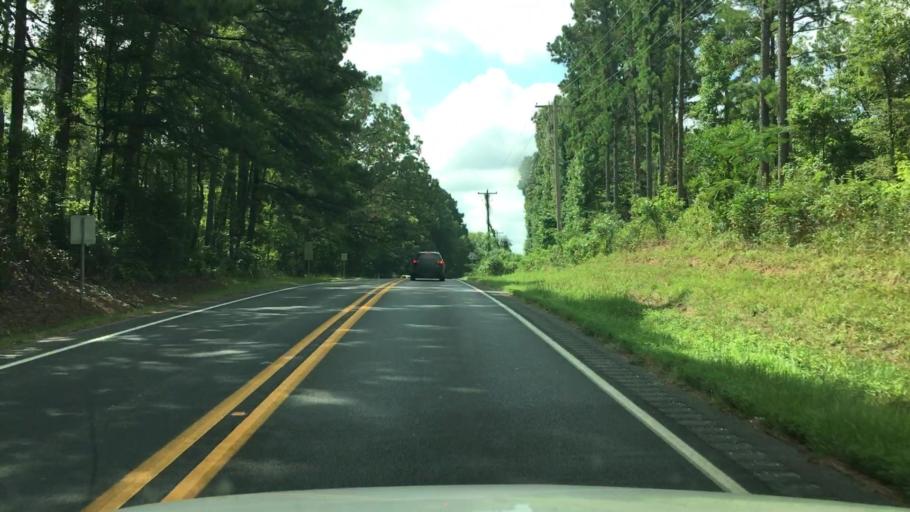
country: US
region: Arkansas
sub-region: Garland County
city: Lake Hamilton
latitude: 34.3116
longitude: -93.1689
